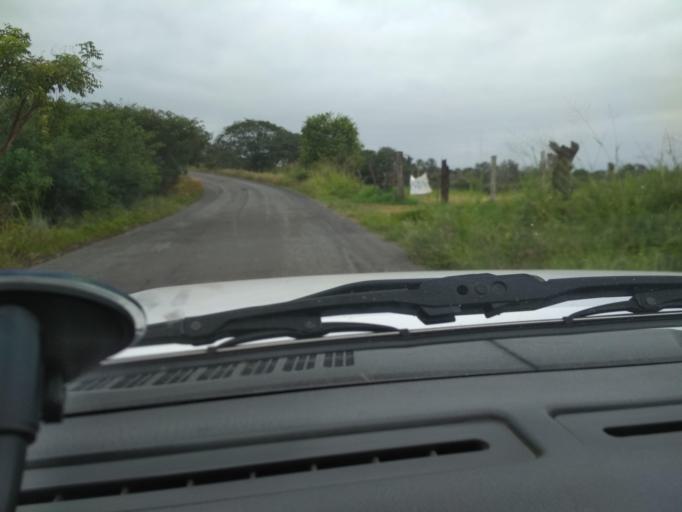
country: MX
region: Veracruz
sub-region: Emiliano Zapata
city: Dos Rios
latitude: 19.5311
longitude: -96.7985
